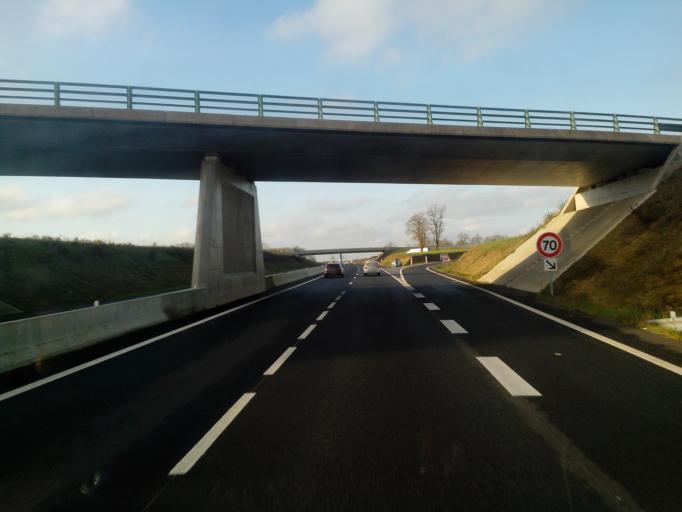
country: FR
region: Pays de la Loire
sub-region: Departement de Maine-et-Loire
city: La Tessoualle
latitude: 47.0224
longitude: -0.8815
